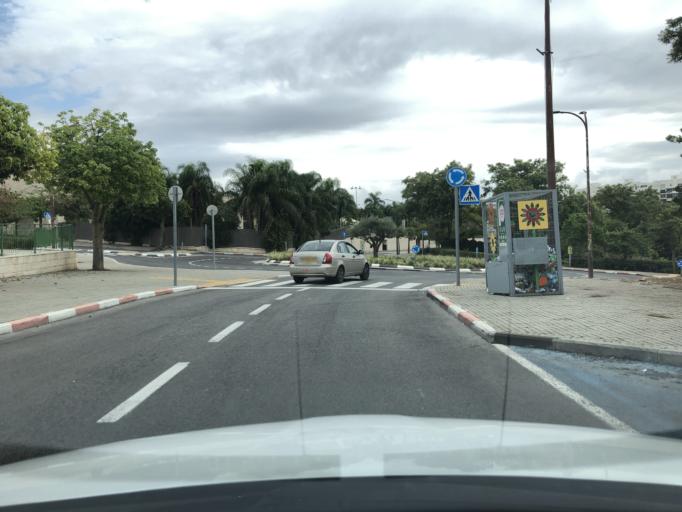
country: IL
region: Central District
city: Modiin
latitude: 31.8995
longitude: 35.0155
